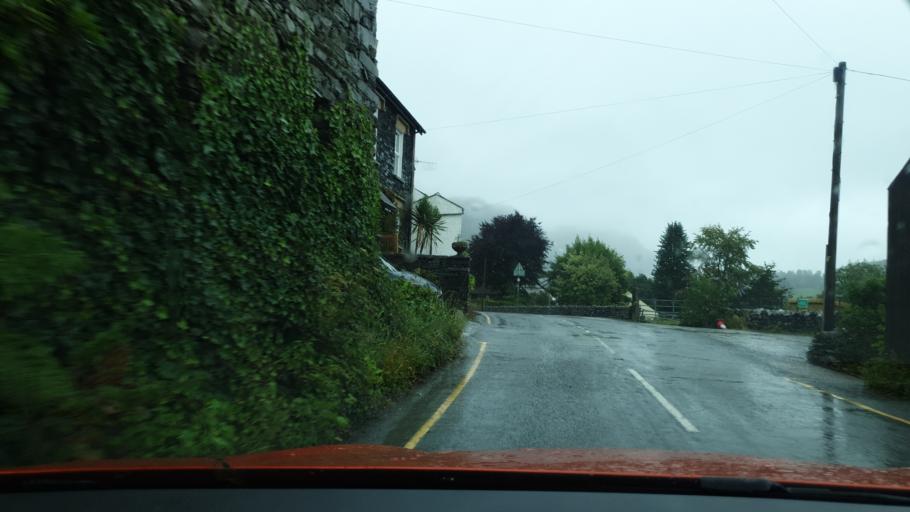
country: GB
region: England
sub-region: Cumbria
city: Ambleside
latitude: 54.3656
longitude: -3.0766
